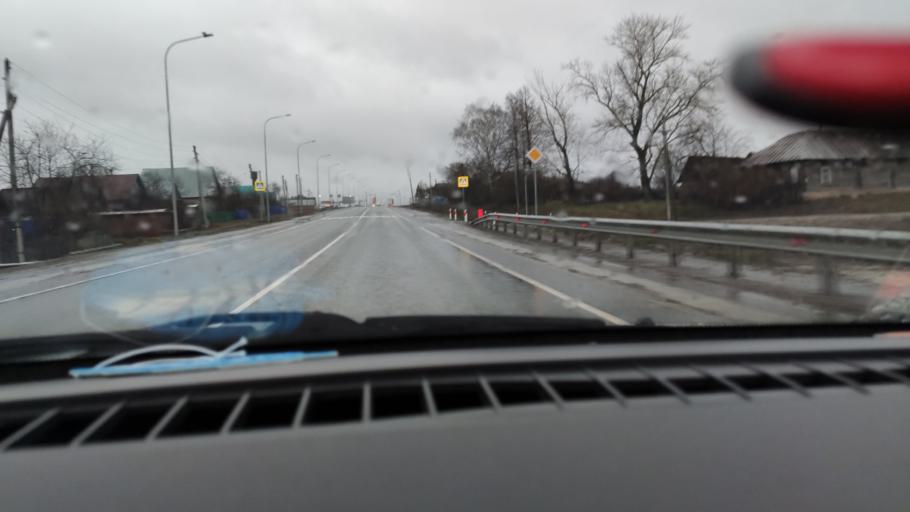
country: RU
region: Tatarstan
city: Mendeleyevsk
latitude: 56.0287
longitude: 52.3725
